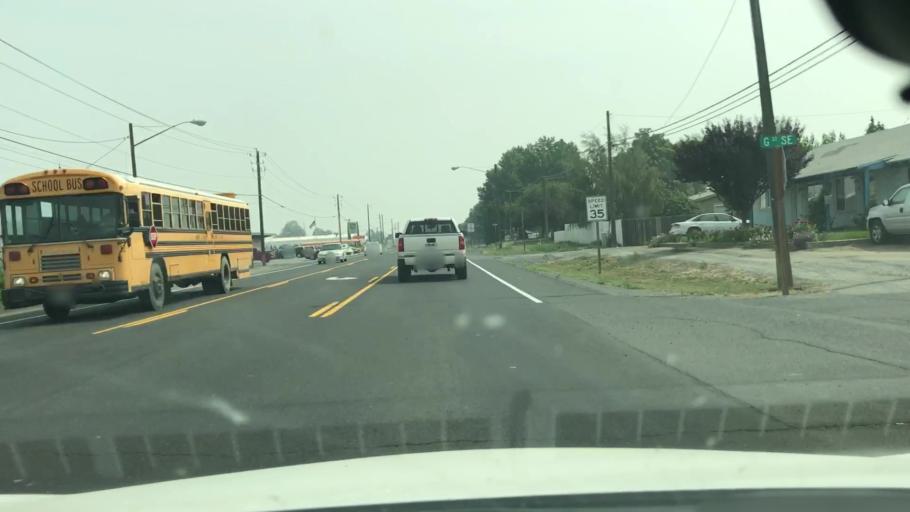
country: US
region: Washington
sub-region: Grant County
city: Quincy
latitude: 47.2340
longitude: -119.8412
